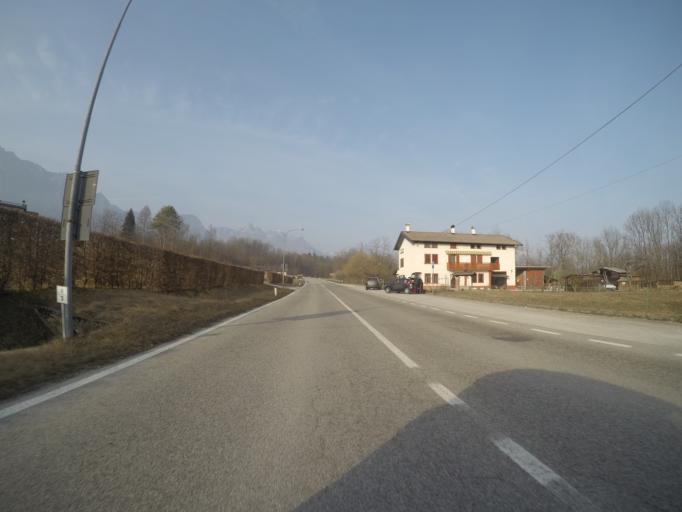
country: IT
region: Veneto
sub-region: Provincia di Belluno
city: Sedico
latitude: 46.1160
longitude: 12.0754
